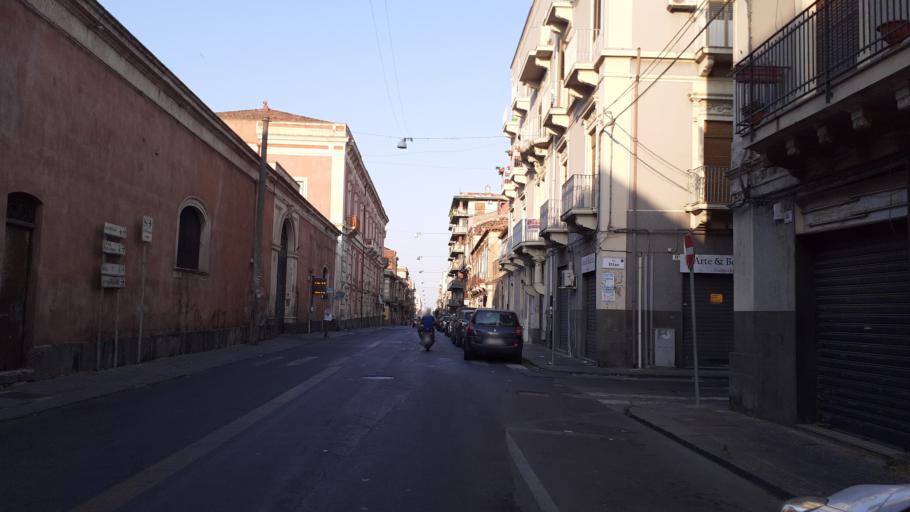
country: IT
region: Sicily
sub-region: Catania
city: Catania
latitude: 37.5013
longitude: 15.0740
